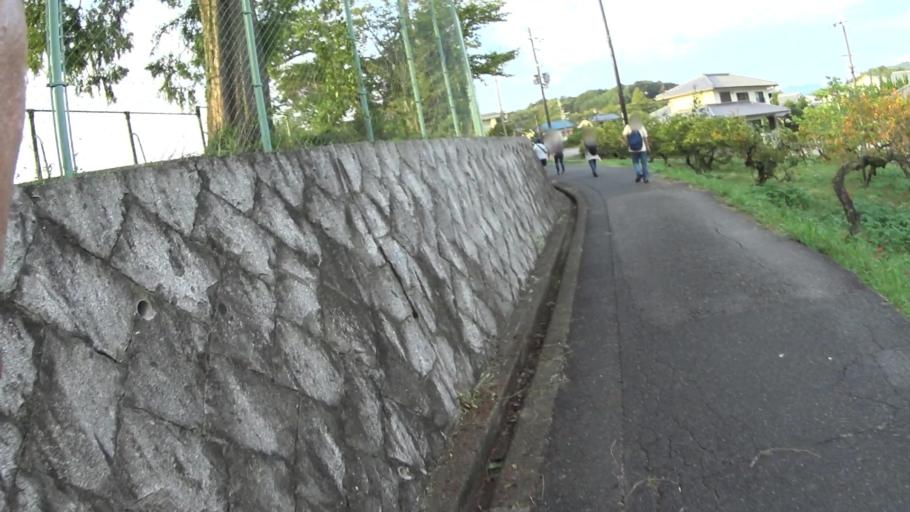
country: JP
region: Nara
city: Kashihara-shi
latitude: 34.4693
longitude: 135.8068
